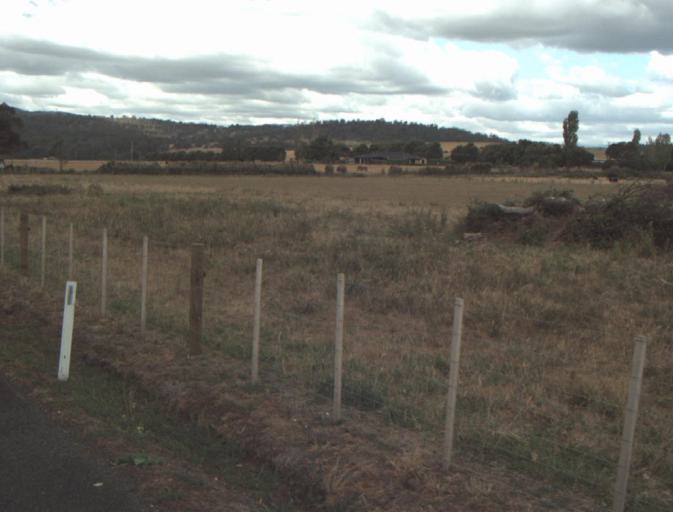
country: AU
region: Tasmania
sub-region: Launceston
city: Mayfield
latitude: -41.2870
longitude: 146.9971
